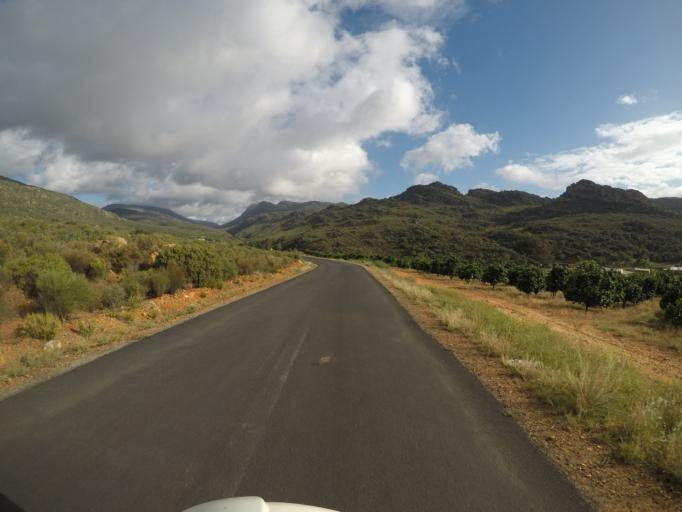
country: ZA
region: Western Cape
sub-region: West Coast District Municipality
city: Clanwilliam
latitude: -32.4231
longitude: 18.9340
